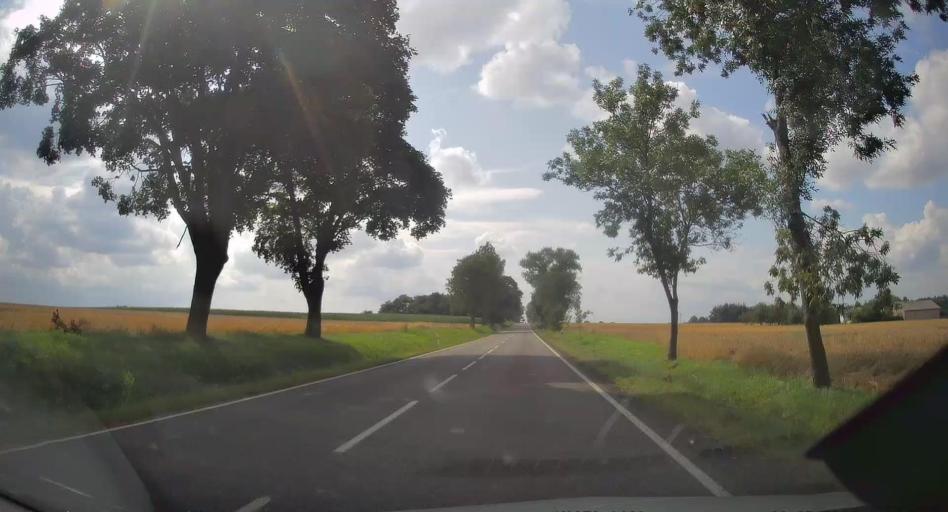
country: PL
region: Lodz Voivodeship
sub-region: Powiat brzezinski
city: Jezow
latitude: 51.8094
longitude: 20.0057
